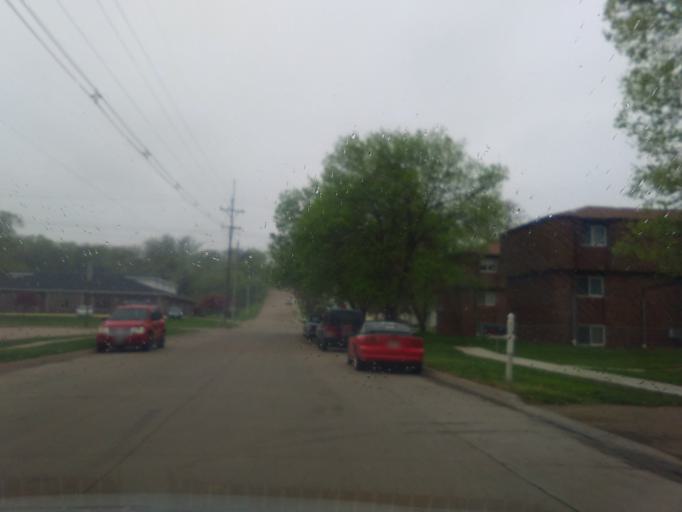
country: US
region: Nebraska
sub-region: Madison County
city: Norfolk
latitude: 42.0382
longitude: -97.4167
